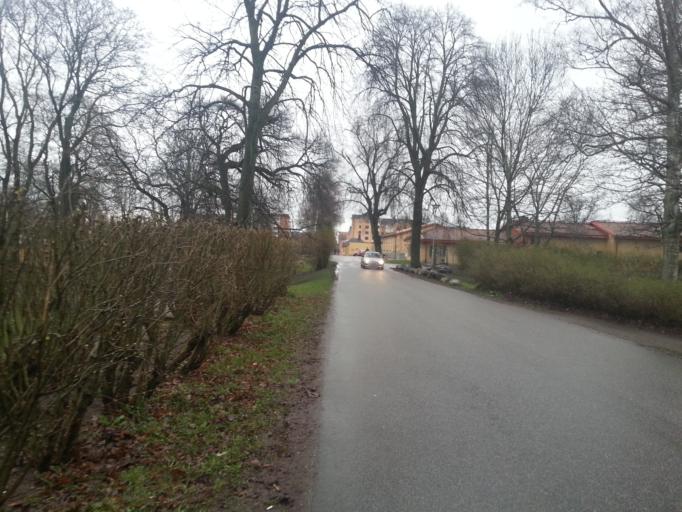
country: SE
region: OEstergoetland
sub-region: Norrkopings Kommun
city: Norrkoping
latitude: 58.5899
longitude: 16.1671
